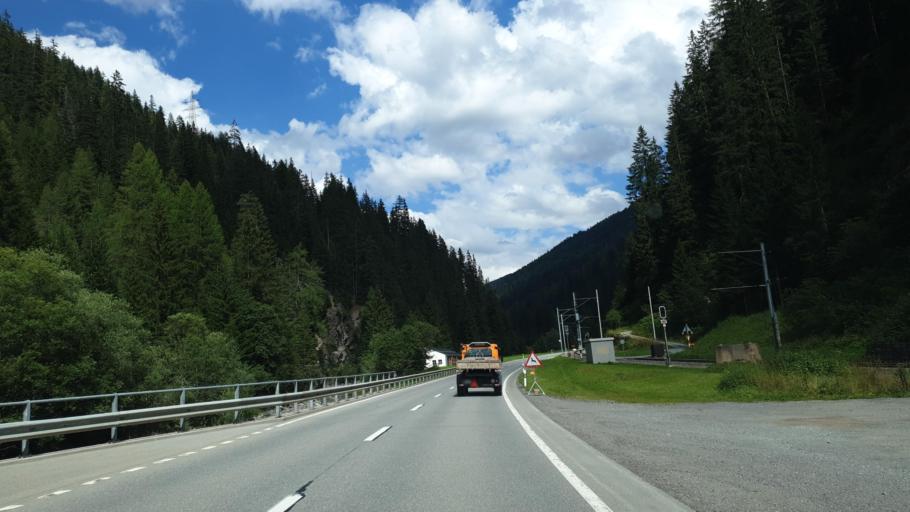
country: CH
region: Grisons
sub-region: Plessur District
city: Arosa
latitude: 46.7167
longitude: 9.7604
